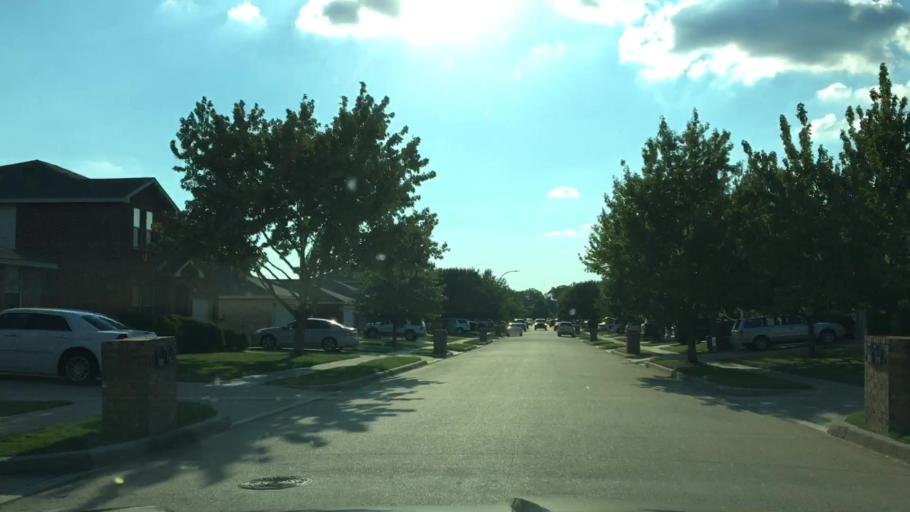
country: US
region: Texas
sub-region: Denton County
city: Justin
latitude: 33.0396
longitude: -97.3158
